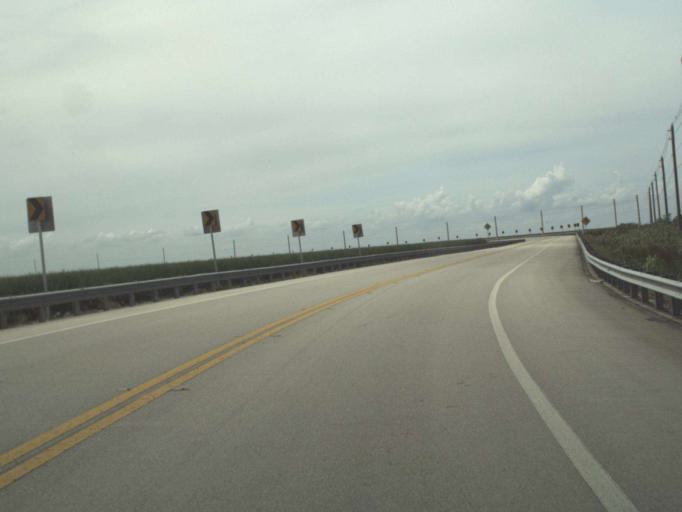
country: US
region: Florida
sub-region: Palm Beach County
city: Pahokee
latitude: 26.7696
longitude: -80.6550
